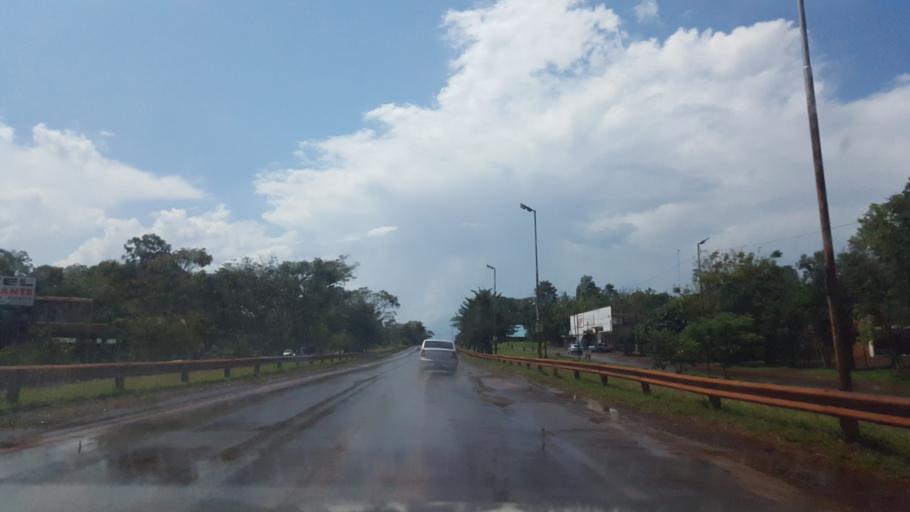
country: AR
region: Misiones
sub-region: Departamento de Eldorado
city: Eldorado
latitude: -26.4012
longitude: -54.6342
